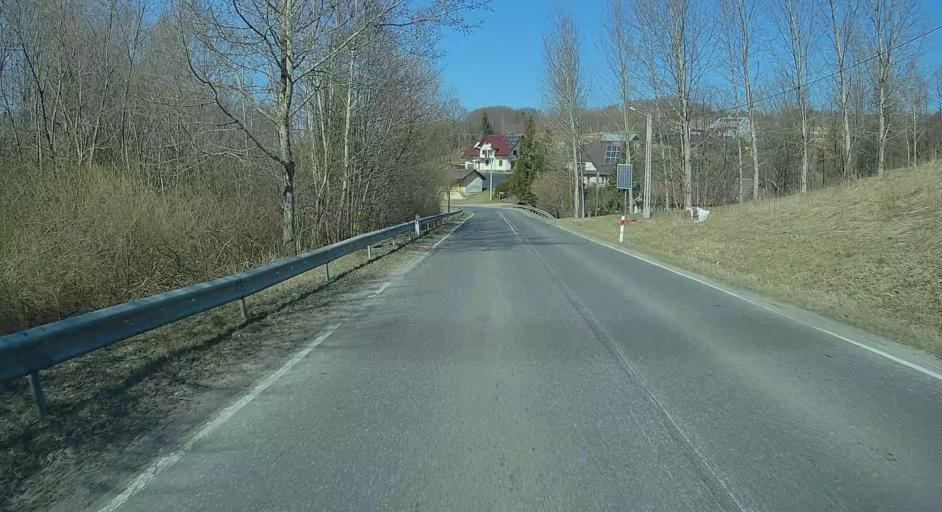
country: PL
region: Subcarpathian Voivodeship
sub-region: Powiat rzeszowski
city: Hyzne
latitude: 49.8984
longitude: 22.2192
